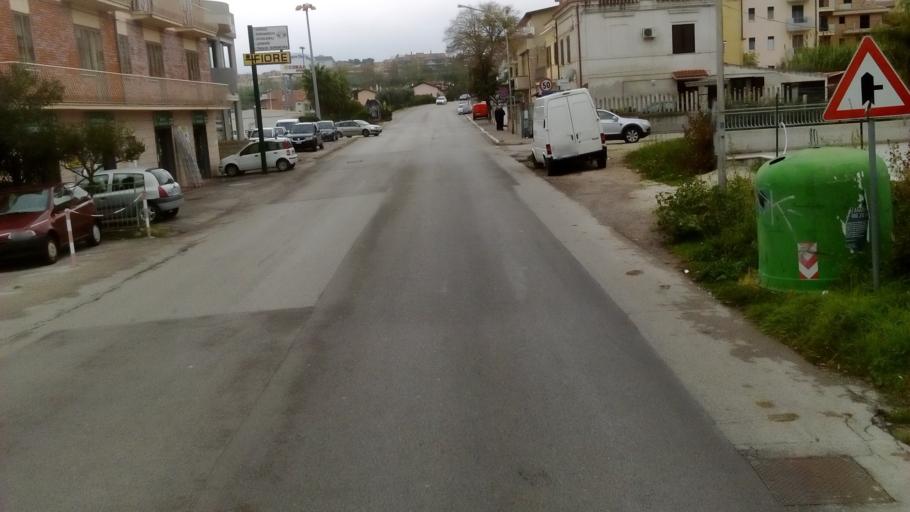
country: IT
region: Abruzzo
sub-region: Provincia di Chieti
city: Vasto
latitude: 42.1004
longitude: 14.7017
